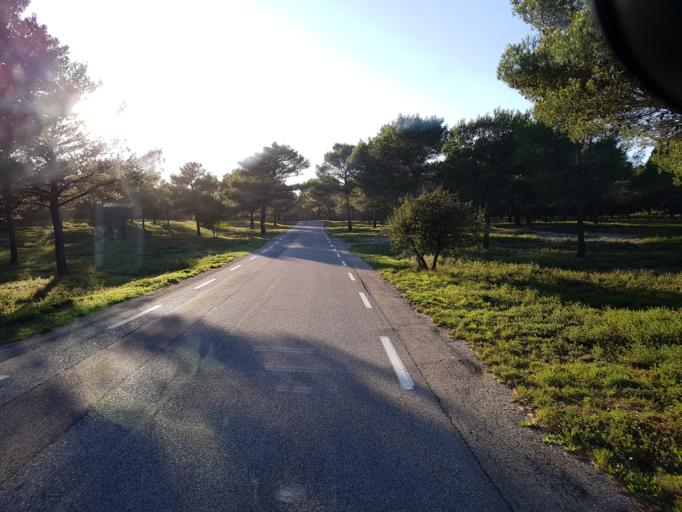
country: FR
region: Provence-Alpes-Cote d'Azur
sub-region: Departement des Bouches-du-Rhone
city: Cuges-les-Pins
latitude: 43.2440
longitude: 5.7185
